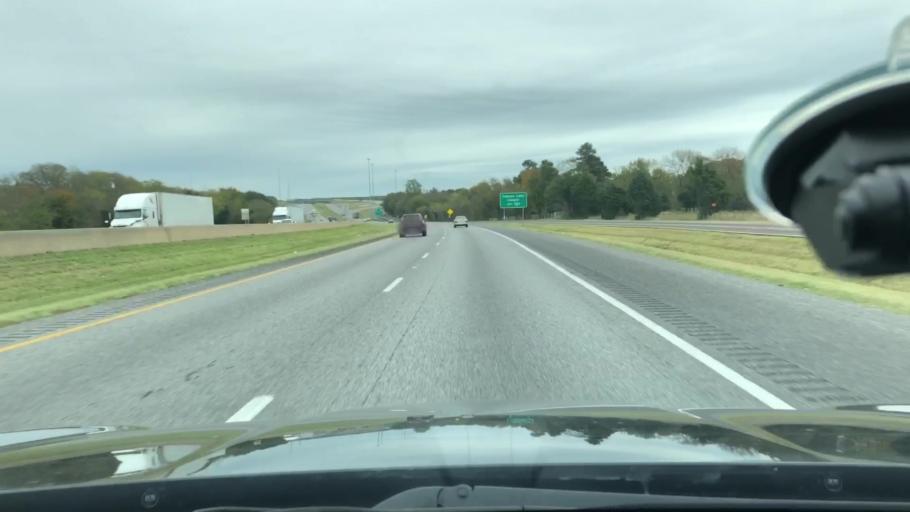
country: US
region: Texas
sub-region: Hunt County
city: Greenville
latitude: 33.1303
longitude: -96.0049
